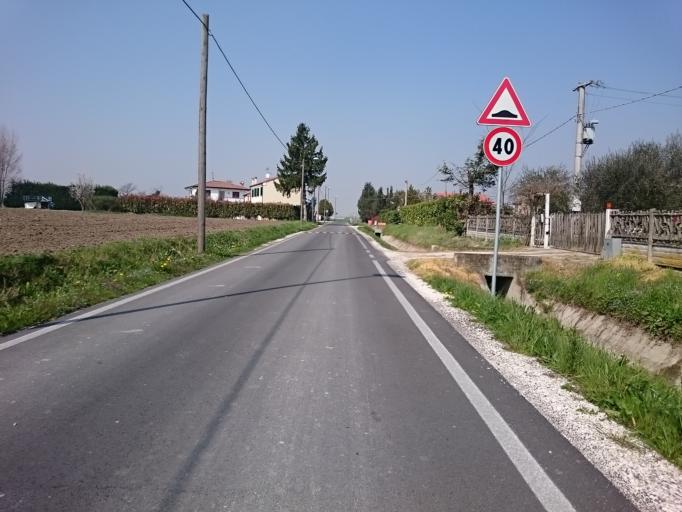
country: IT
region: Veneto
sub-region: Provincia di Padova
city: Villa Estense
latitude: 45.1910
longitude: 11.6740
